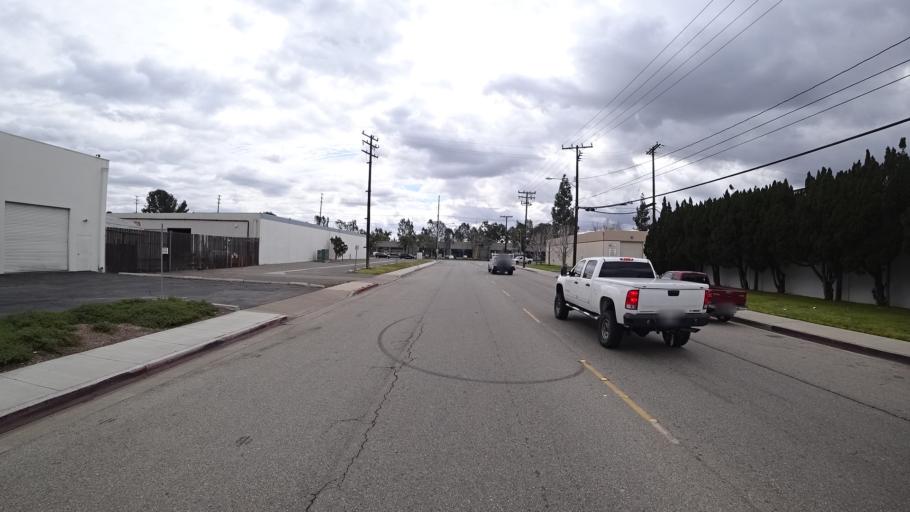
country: US
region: California
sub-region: Orange County
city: Placentia
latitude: 33.8506
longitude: -117.8639
